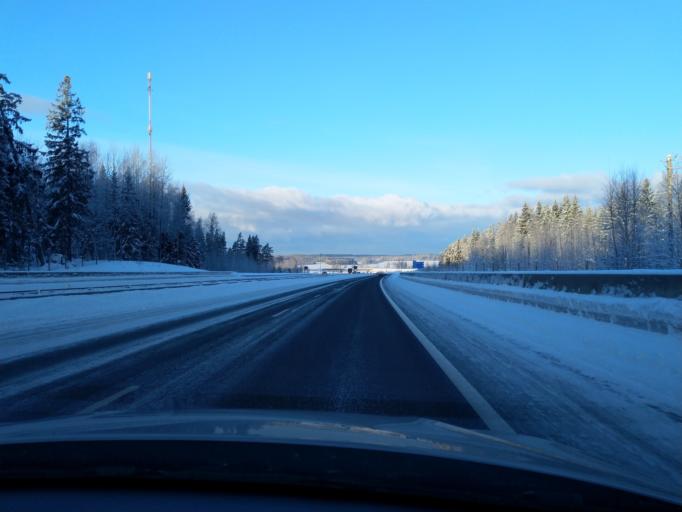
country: FI
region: Varsinais-Suomi
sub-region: Salo
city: Suomusjaervi
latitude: 60.3855
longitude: 23.5979
